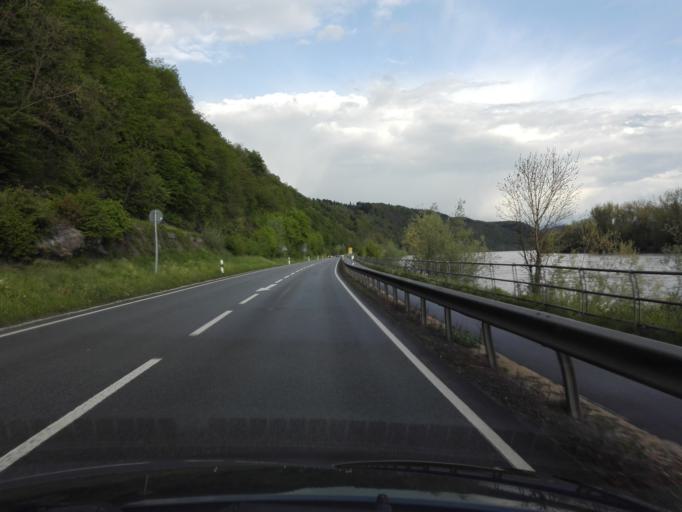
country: DE
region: Bavaria
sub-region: Lower Bavaria
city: Thyrnau
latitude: 48.5916
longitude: 13.5151
